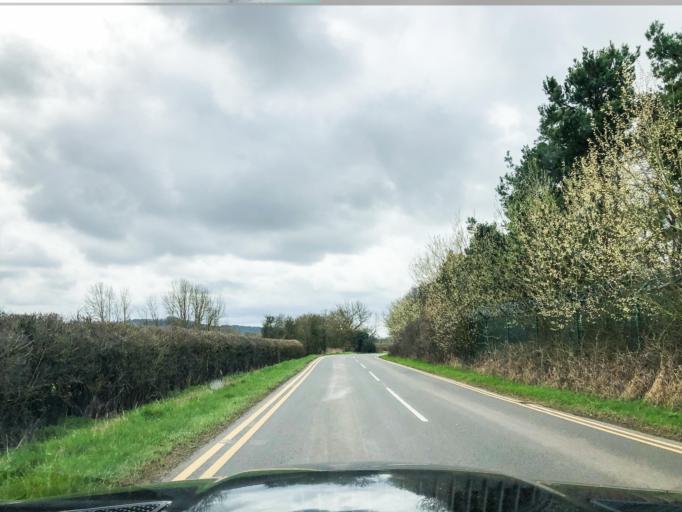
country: GB
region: England
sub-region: Warwickshire
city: Harbury
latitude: 52.1588
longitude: -1.4360
